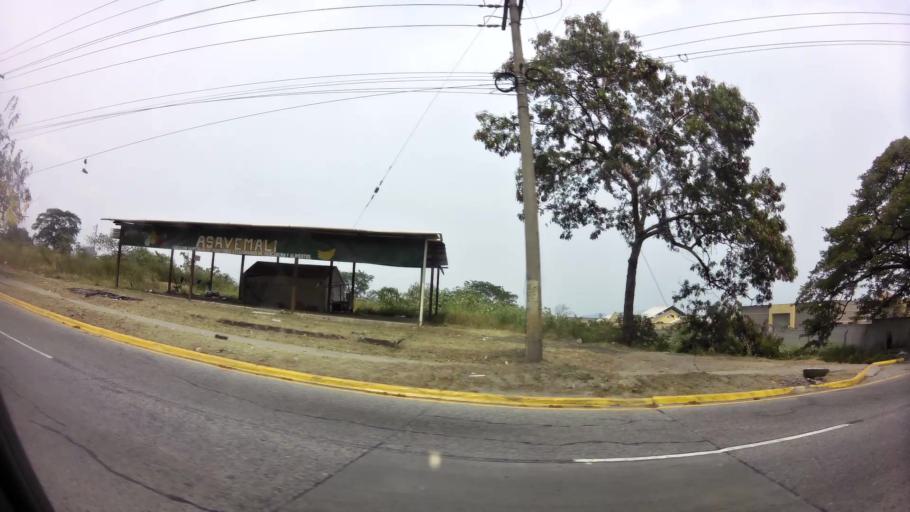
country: HN
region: Cortes
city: Armenta
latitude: 15.4735
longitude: -88.0337
